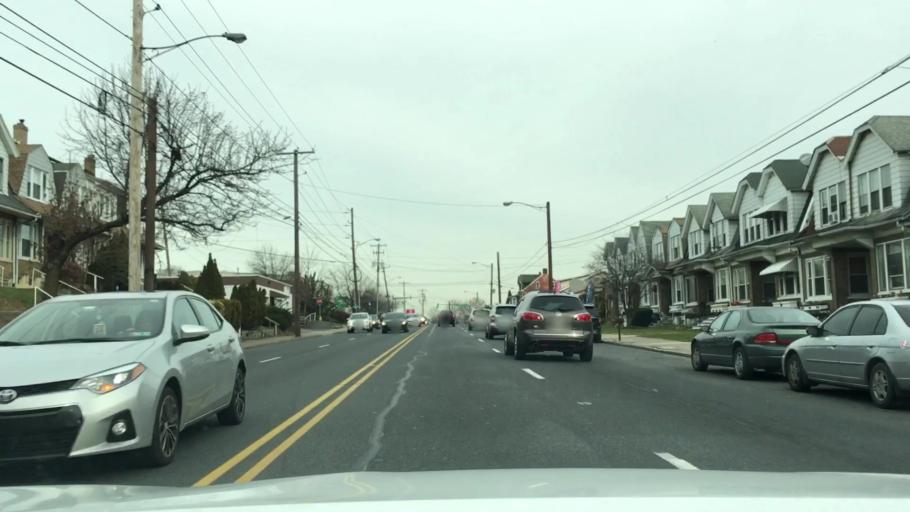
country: US
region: Pennsylvania
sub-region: Lehigh County
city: Fullerton
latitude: 40.6144
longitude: -75.4462
